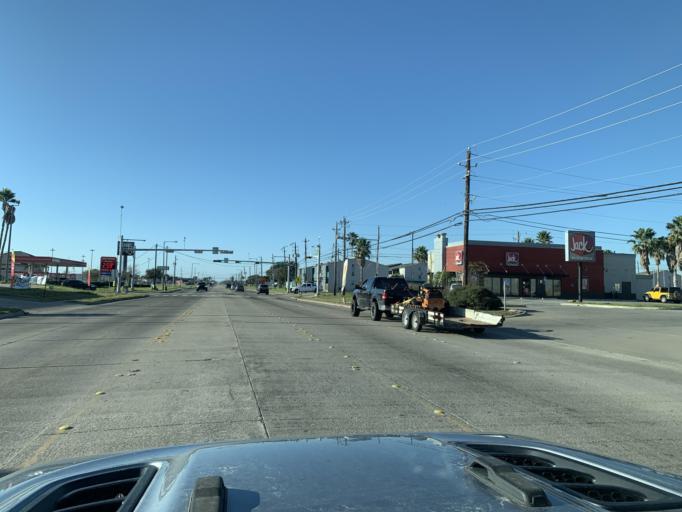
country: US
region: Texas
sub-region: Nueces County
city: Corpus Christi
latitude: 27.6662
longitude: -97.2838
